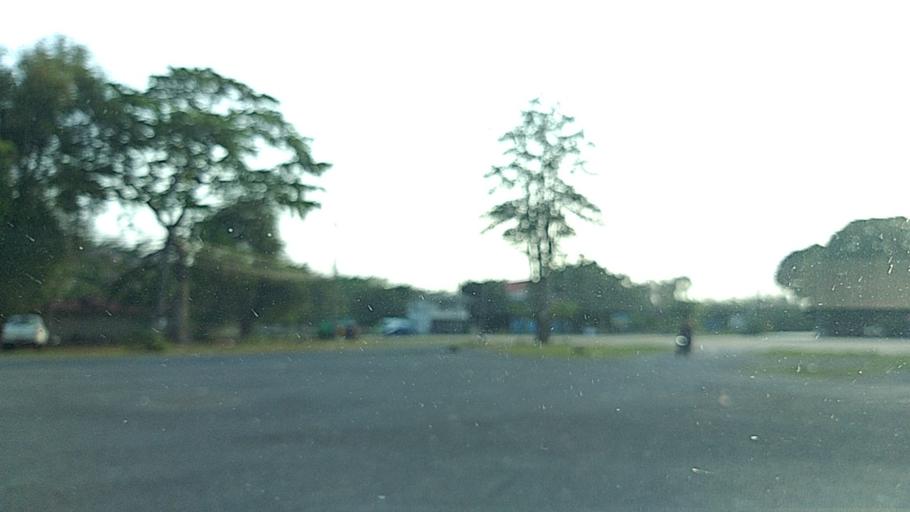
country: TH
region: Sara Buri
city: Saraburi
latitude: 14.4577
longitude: 100.9480
